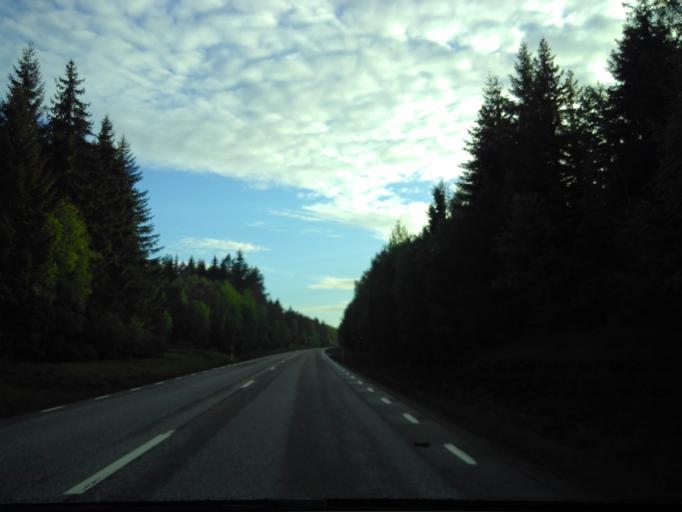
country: SE
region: Vaestra Goetaland
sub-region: Herrljunga Kommun
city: Herrljunga
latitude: 58.0596
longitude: 13.0658
